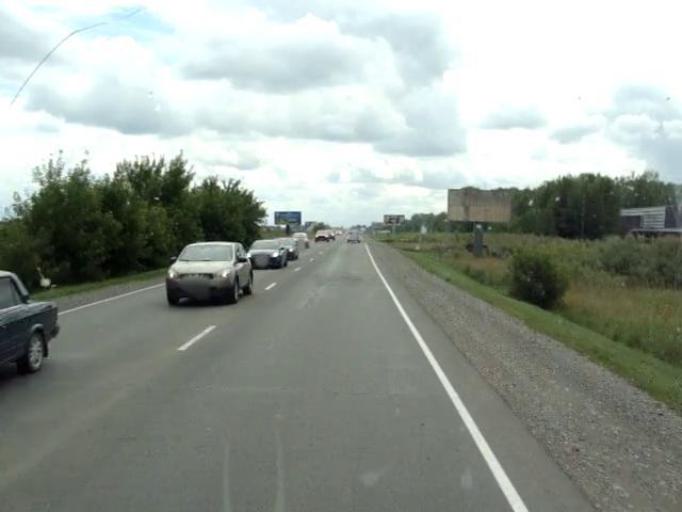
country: RU
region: Altai Krai
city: Zarya
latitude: 52.5734
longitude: 85.1820
